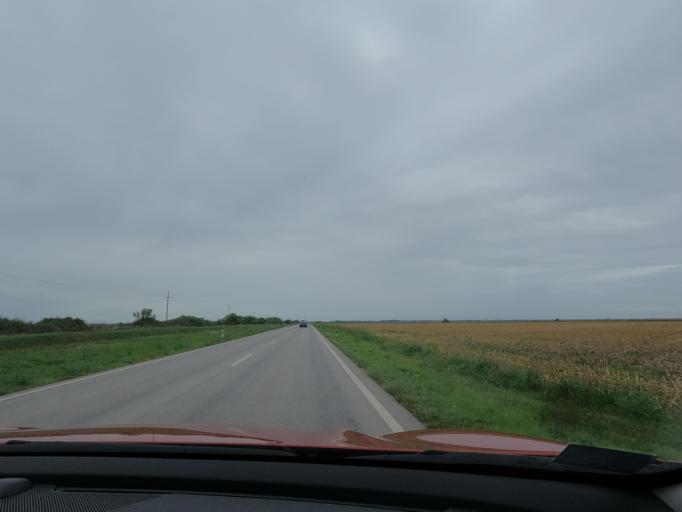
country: RS
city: Banatska Topola
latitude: 45.7459
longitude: 20.4210
